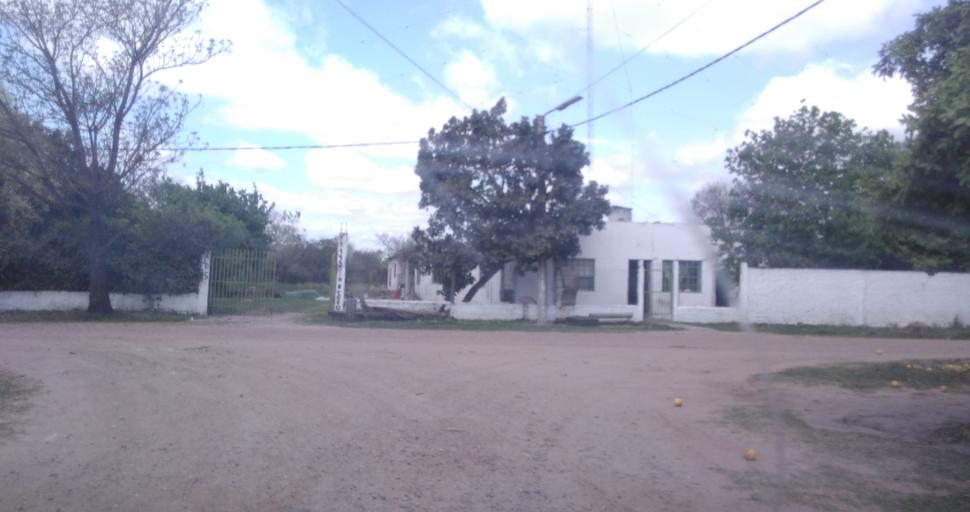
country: AR
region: Chaco
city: Fontana
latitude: -27.4278
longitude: -59.0324
